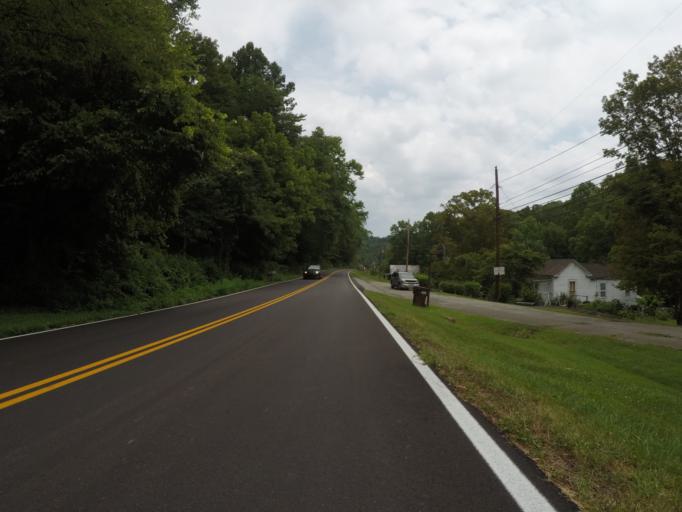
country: US
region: Kentucky
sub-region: Boyd County
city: Catlettsburg
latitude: 38.4185
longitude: -82.6176
